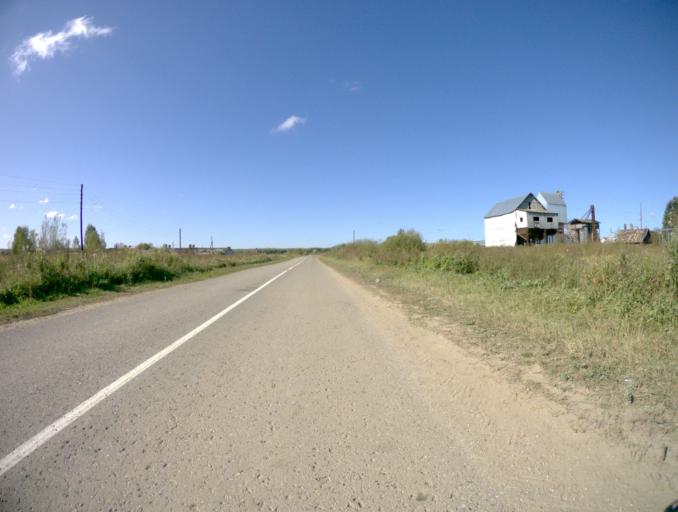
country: RU
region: Vladimir
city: Kameshkovo
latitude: 56.3596
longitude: 40.8914
